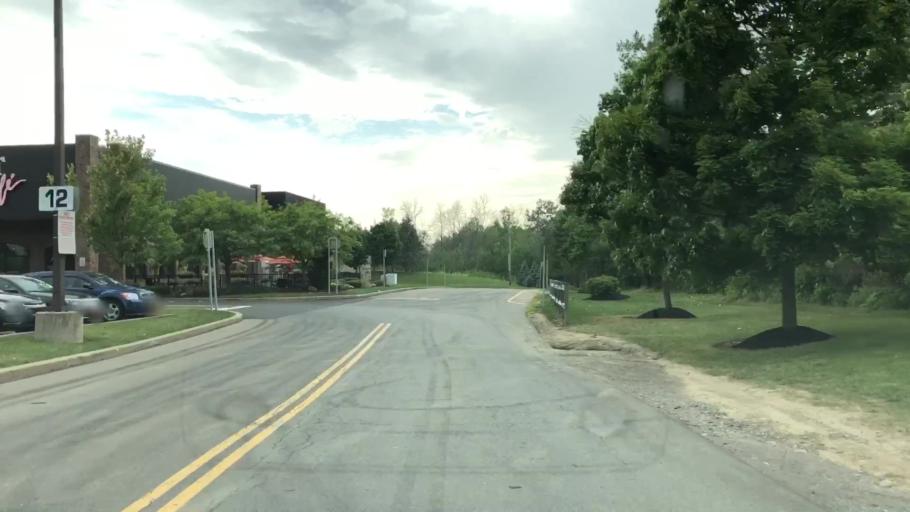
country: US
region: New York
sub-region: Erie County
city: Depew
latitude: 42.8824
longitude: -78.6992
